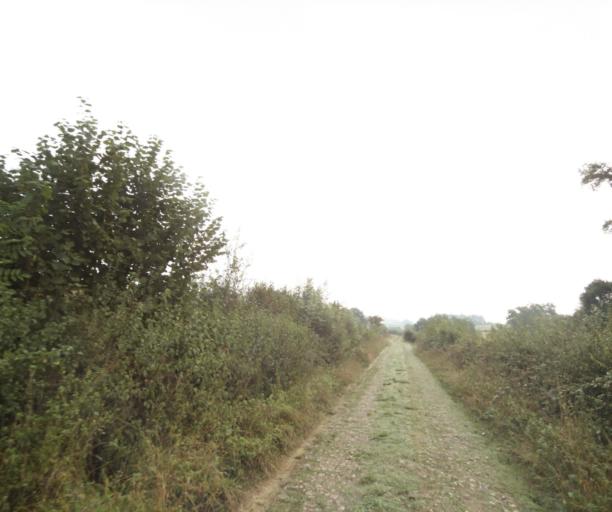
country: FR
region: Bourgogne
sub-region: Departement de Saone-et-Loire
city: Charolles
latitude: 46.4312
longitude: 4.3008
